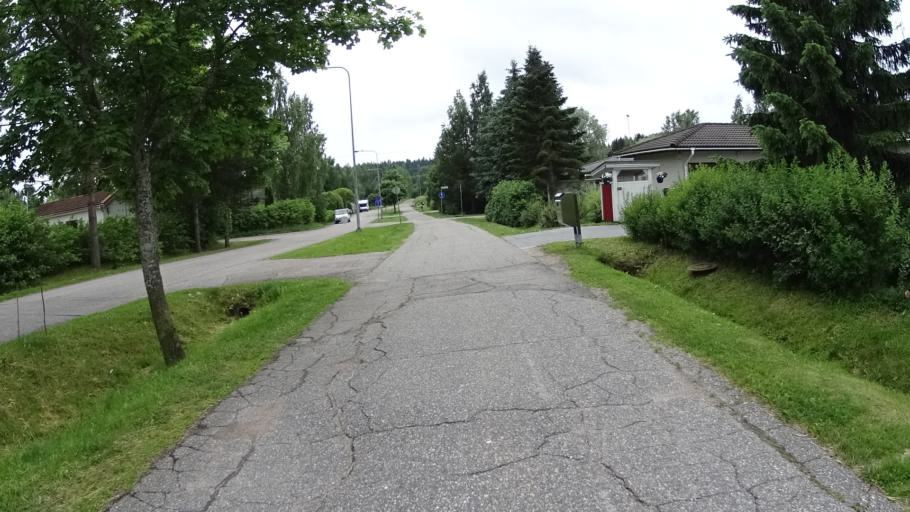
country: FI
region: Uusimaa
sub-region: Helsinki
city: Helsinki
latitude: 60.2754
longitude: 24.9127
